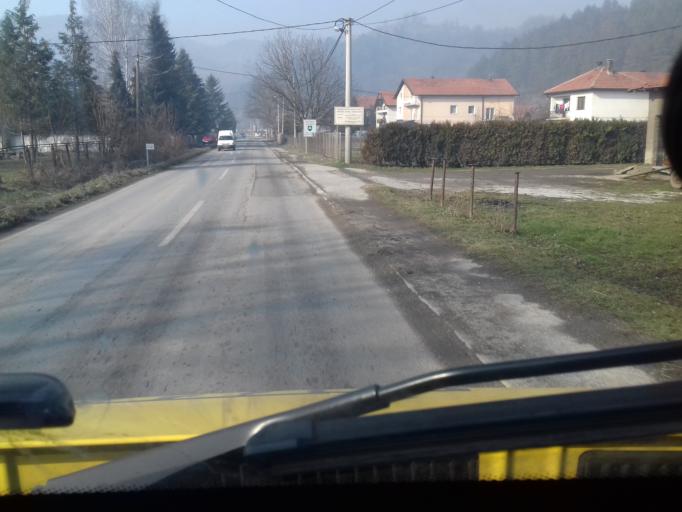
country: BA
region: Federation of Bosnia and Herzegovina
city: Mahala
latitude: 43.9956
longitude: 18.2200
